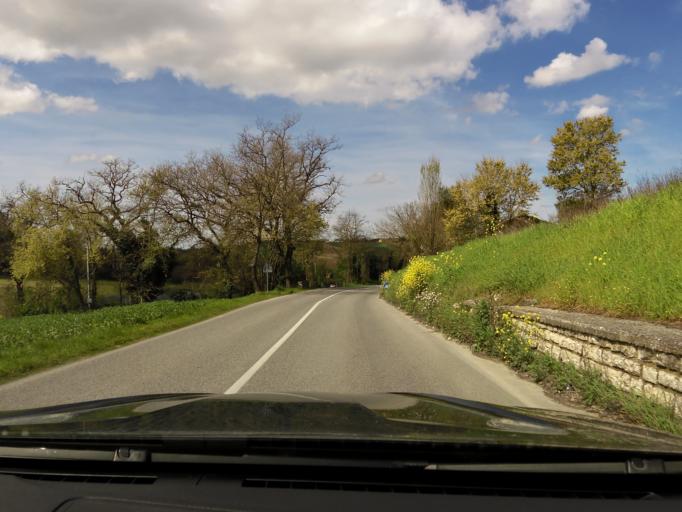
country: IT
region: The Marches
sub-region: Provincia di Ancona
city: Castelfidardo
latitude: 43.4792
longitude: 13.5557
